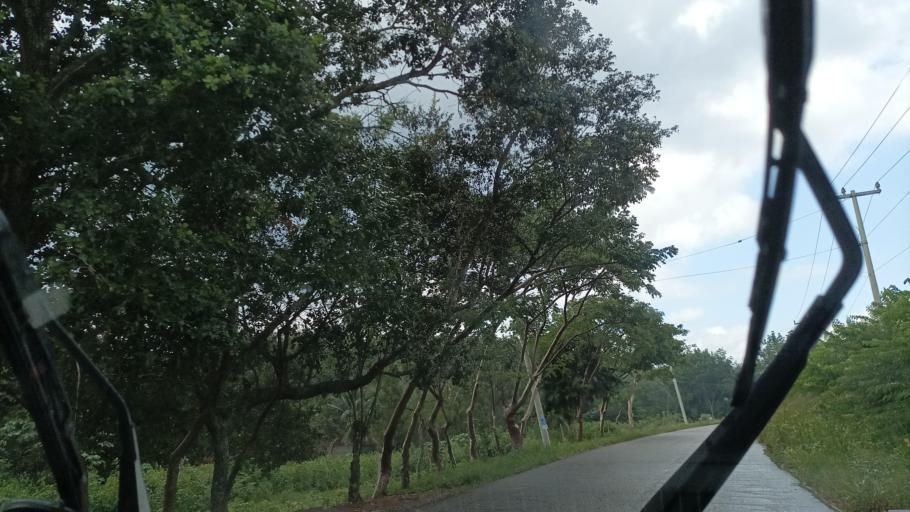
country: MX
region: Veracruz
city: Las Choapas
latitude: 17.8486
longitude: -94.1061
